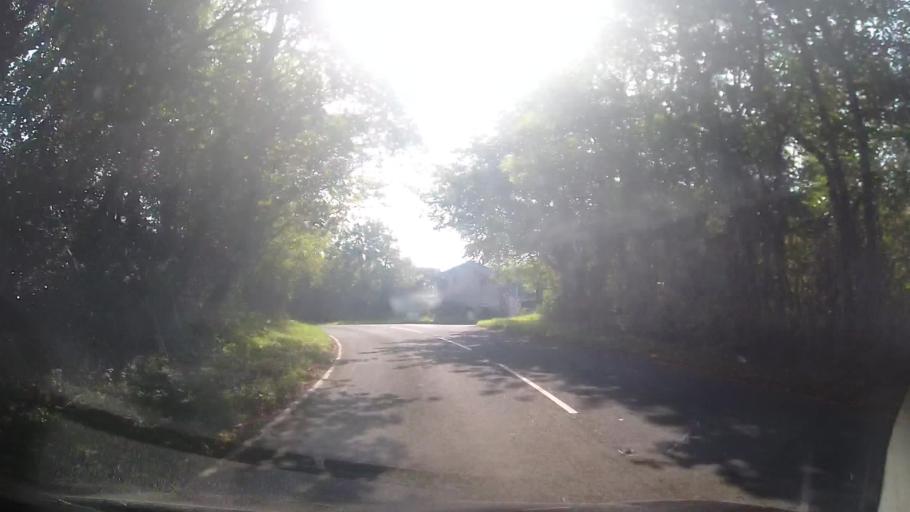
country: GB
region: Wales
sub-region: Pembrokeshire
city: Scleddau
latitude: 51.9812
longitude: -5.0073
